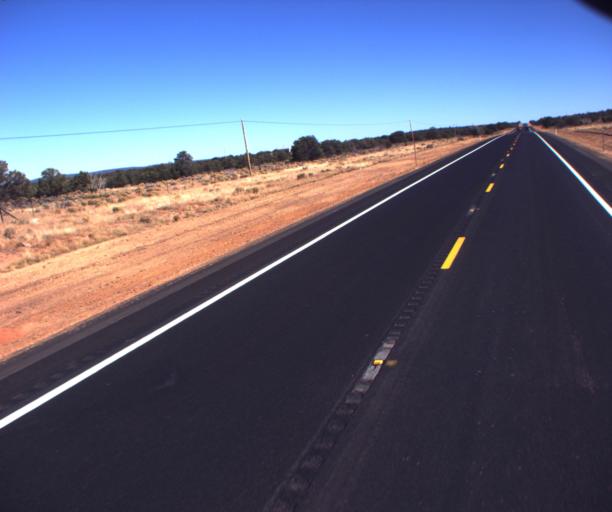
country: US
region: Arizona
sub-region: Apache County
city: Ganado
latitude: 35.7178
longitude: -109.3989
